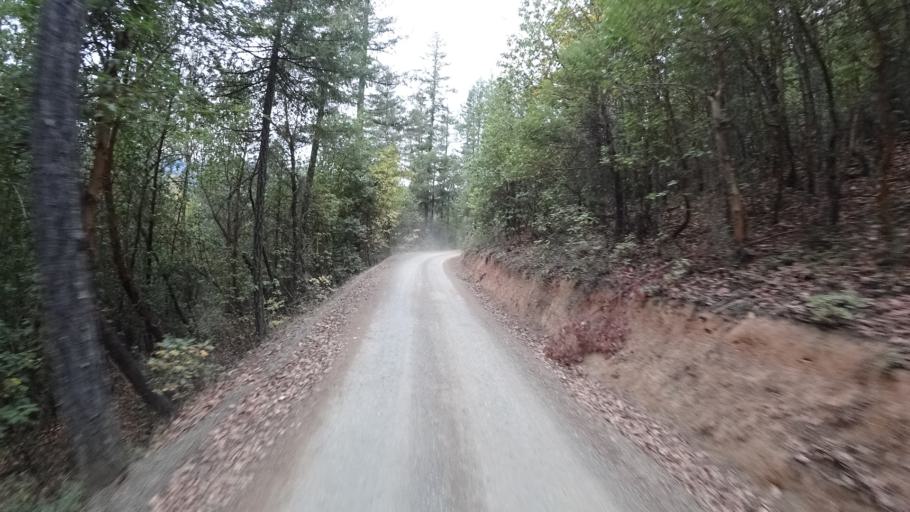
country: US
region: California
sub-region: Siskiyou County
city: Happy Camp
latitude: 41.7835
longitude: -123.3332
